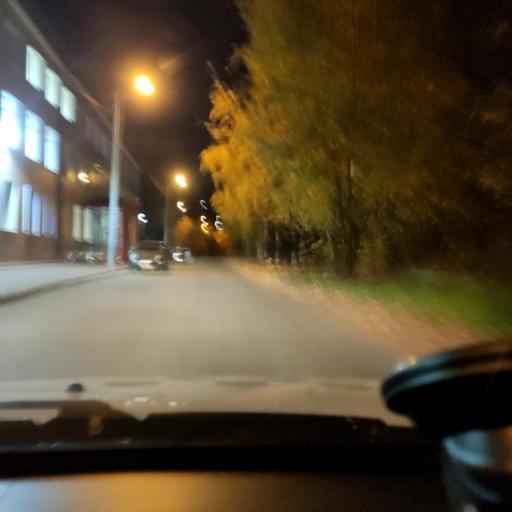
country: RU
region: Perm
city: Perm
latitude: 58.0165
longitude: 56.2752
